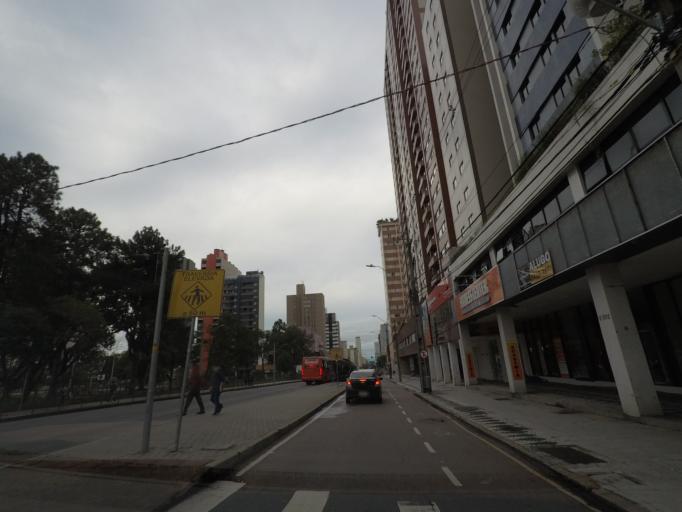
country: BR
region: Parana
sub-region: Curitiba
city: Curitiba
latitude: -25.4414
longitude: -49.2763
